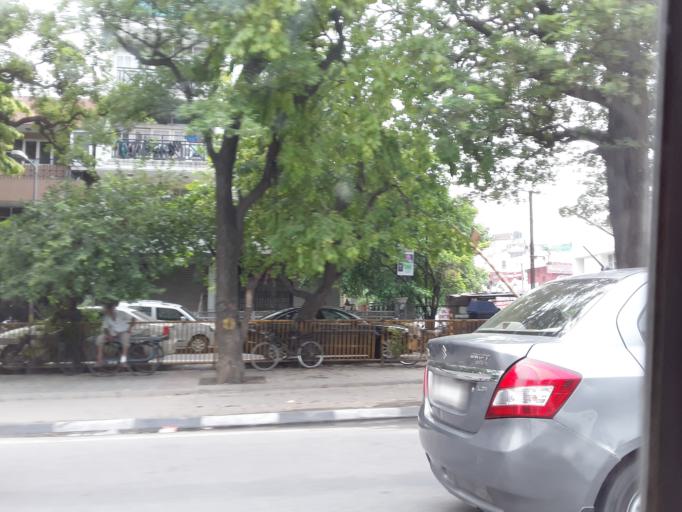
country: IN
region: NCT
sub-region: New Delhi
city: New Delhi
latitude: 28.5439
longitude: 77.2308
